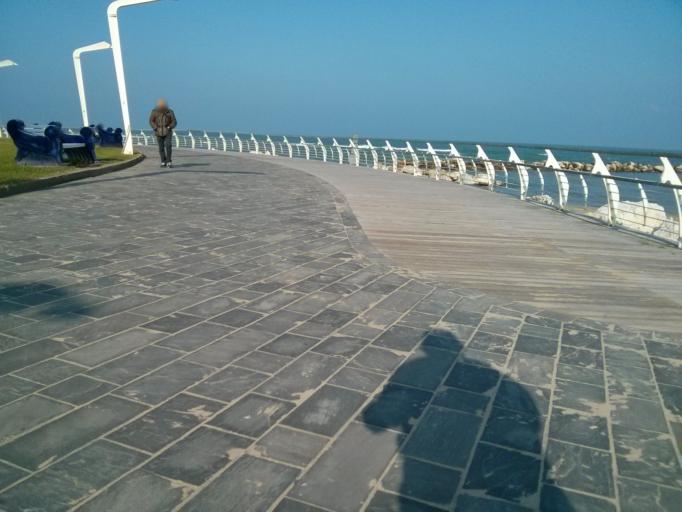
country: IT
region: The Marches
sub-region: Provincia di Pesaro e Urbino
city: Pesaro
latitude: 43.9140
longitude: 12.9192
